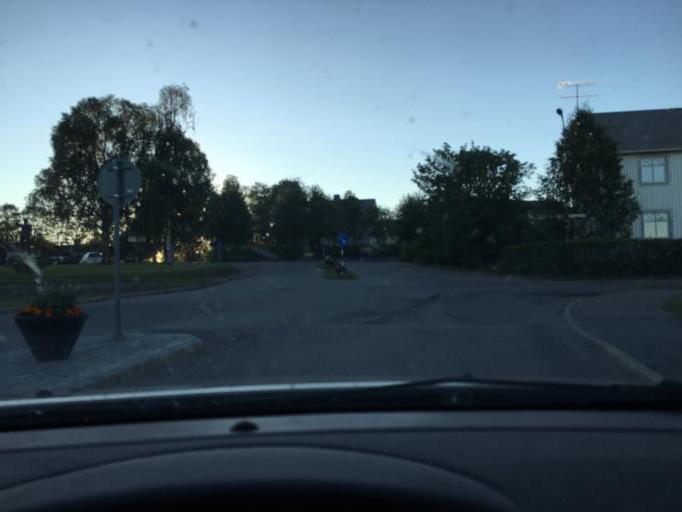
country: SE
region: Norrbotten
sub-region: Kalix Kommun
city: Rolfs
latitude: 65.8540
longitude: 23.1347
